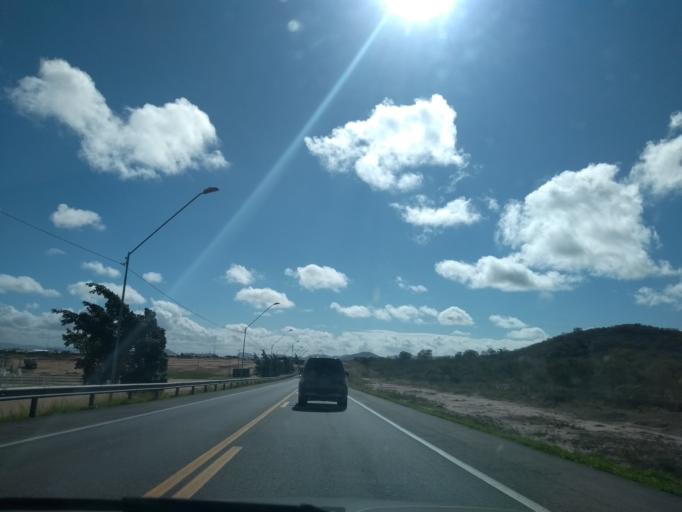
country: BR
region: Bahia
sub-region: Amargosa
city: Amargosa
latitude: -12.8640
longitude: -39.8534
